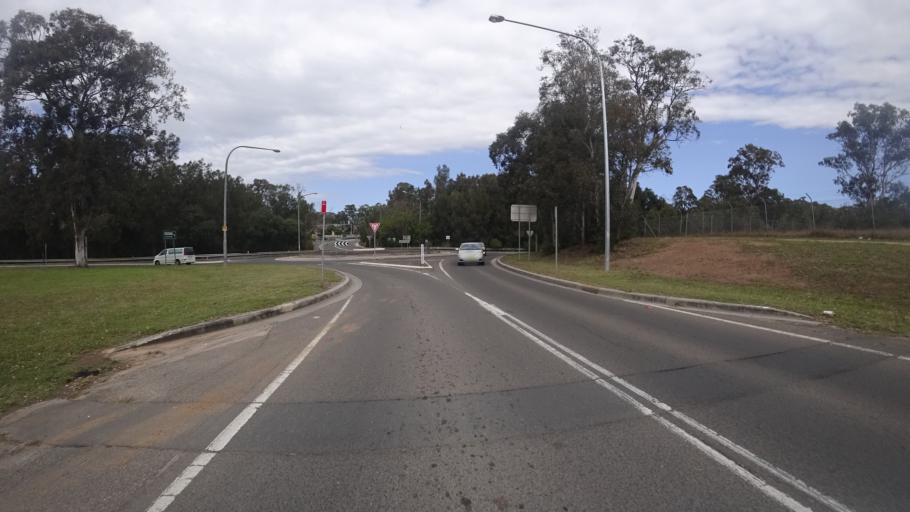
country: AU
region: New South Wales
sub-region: Campbelltown Municipality
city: Glenfield
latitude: -33.9668
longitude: 150.8968
